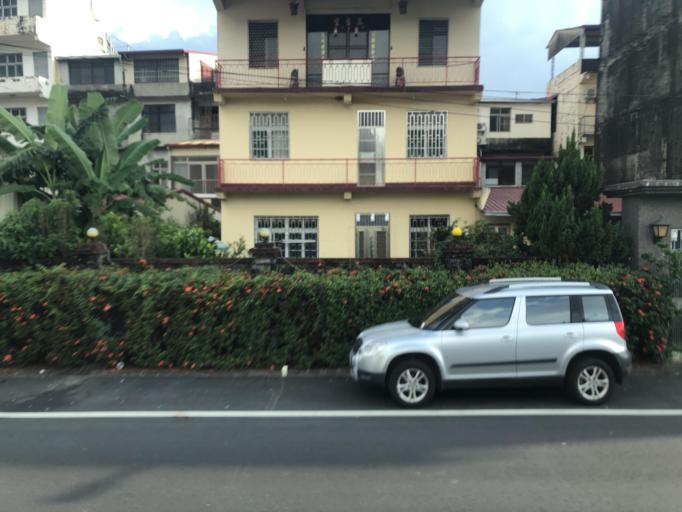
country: TW
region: Taiwan
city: Yujing
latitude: 22.9021
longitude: 120.5399
